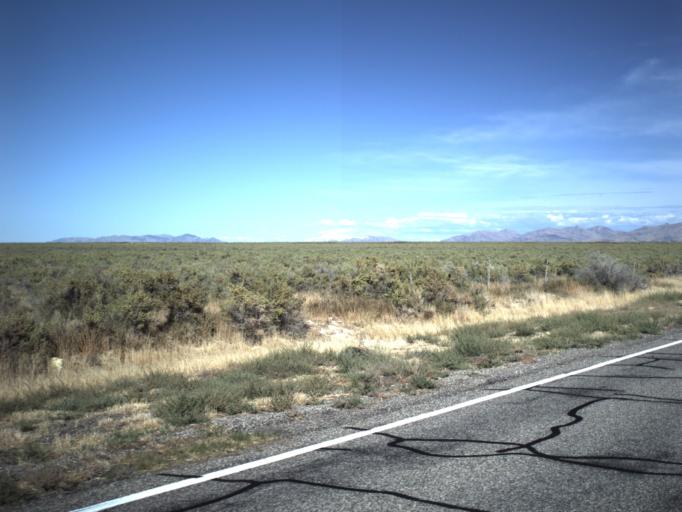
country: US
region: Utah
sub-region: Millard County
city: Delta
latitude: 39.3531
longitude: -112.5164
